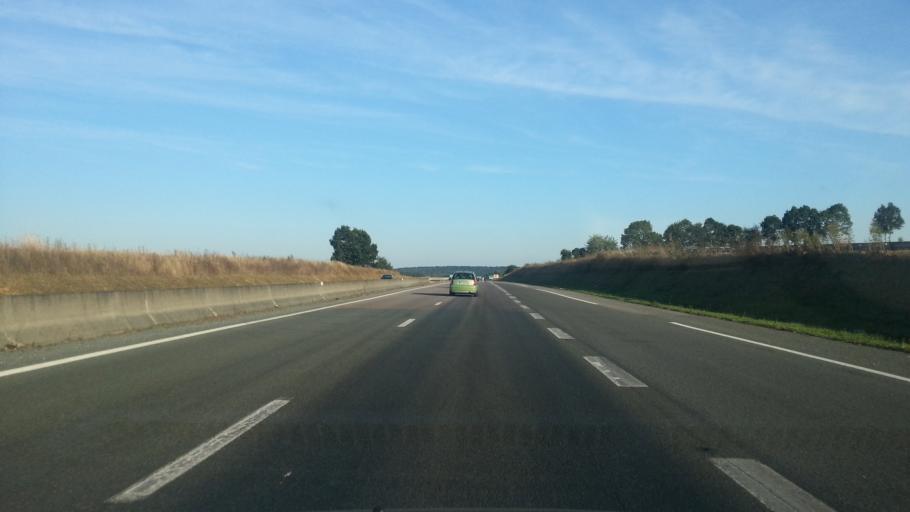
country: FR
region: Picardie
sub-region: Departement de l'Oise
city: Warluis
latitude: 49.4177
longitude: 2.1696
